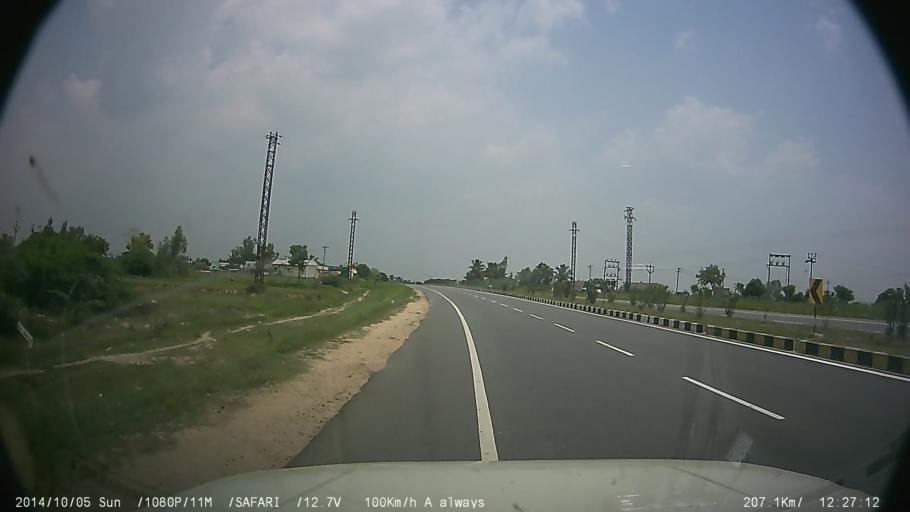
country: IN
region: Tamil Nadu
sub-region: Villupuram
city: Kallakkurichchi
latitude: 11.7157
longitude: 79.1425
